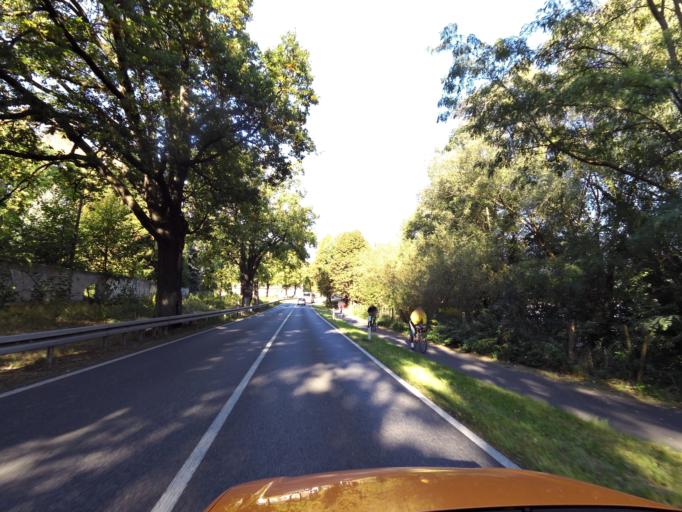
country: DE
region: Brandenburg
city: Potsdam
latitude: 52.4573
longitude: 13.0484
